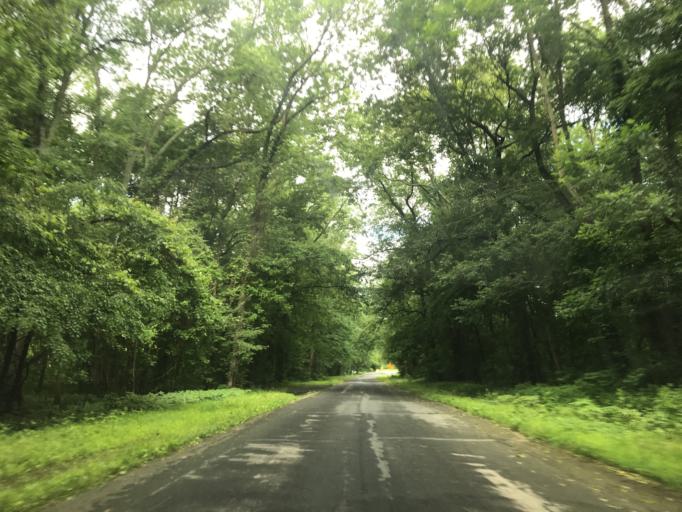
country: US
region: Maryland
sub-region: Caroline County
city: Ridgely
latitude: 38.9201
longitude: -75.9672
